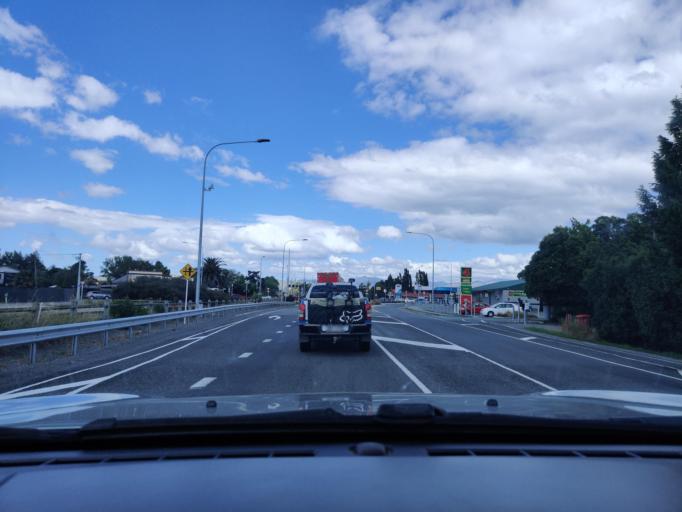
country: NZ
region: Marlborough
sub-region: Marlborough District
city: Blenheim
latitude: -41.4594
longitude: 173.9624
